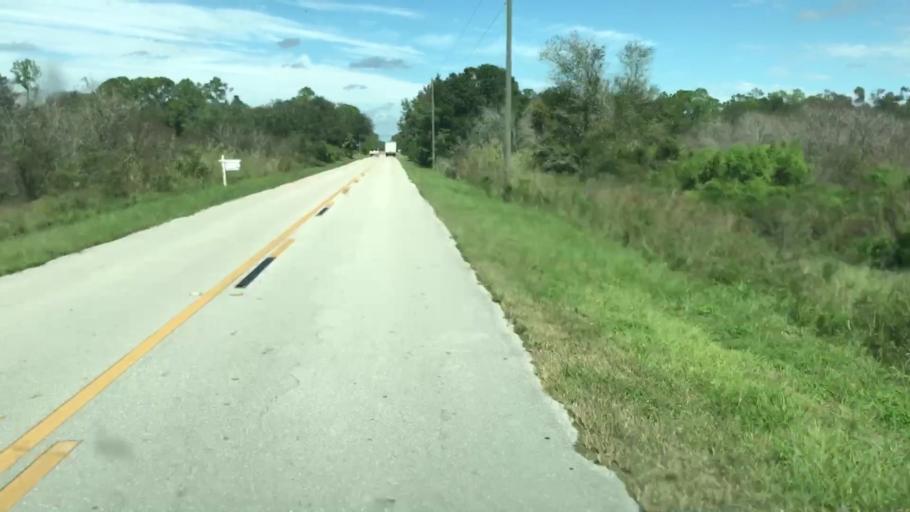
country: US
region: Florida
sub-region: Lee County
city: Lehigh Acres
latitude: 26.6520
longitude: -81.6465
